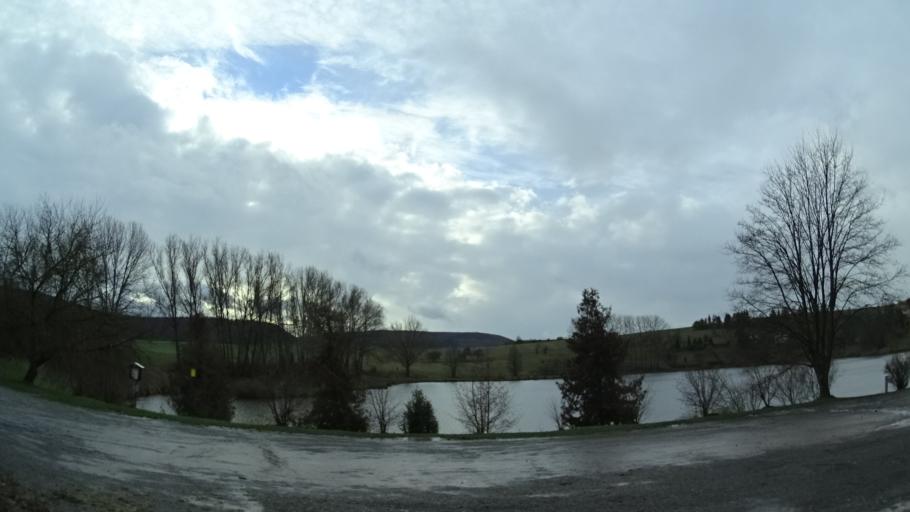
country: DE
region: Thuringia
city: Stepfershausen
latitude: 50.5704
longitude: 10.3048
